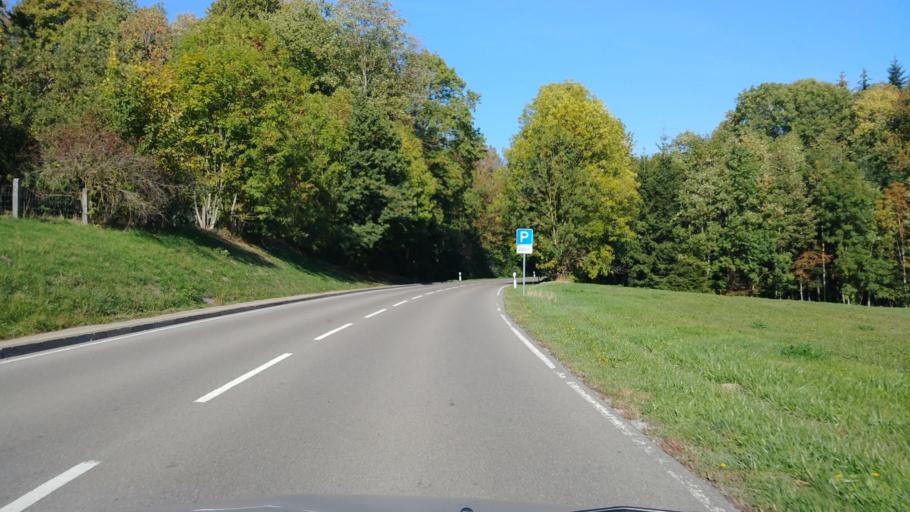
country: DE
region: Baden-Wuerttemberg
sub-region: Regierungsbezirk Stuttgart
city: Gschwend
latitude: 48.9453
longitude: 9.7388
